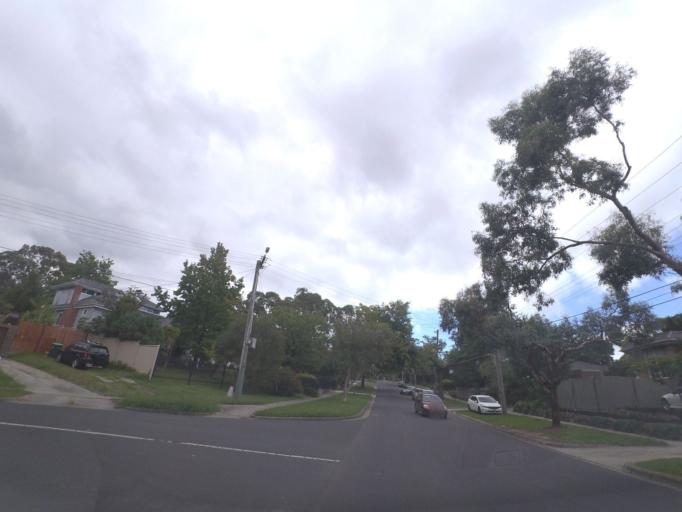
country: AU
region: Victoria
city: Mitcham
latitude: -37.8228
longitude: 145.2088
